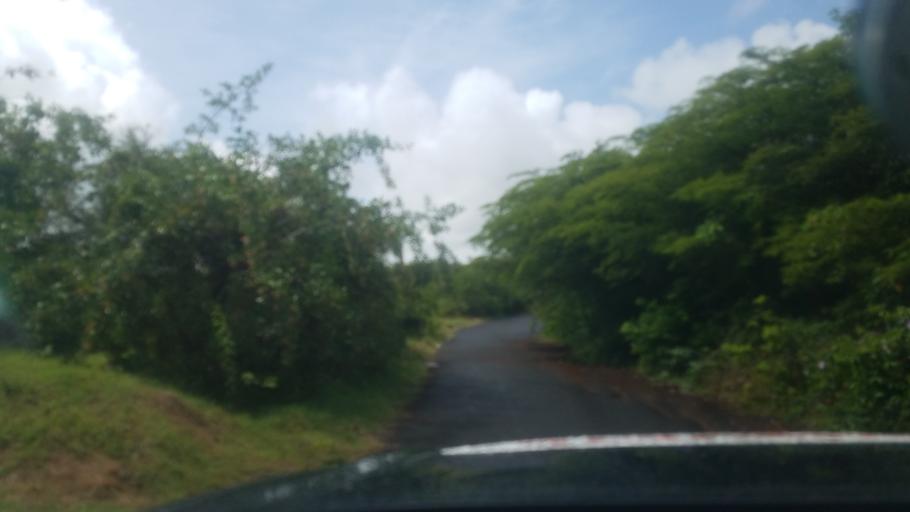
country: LC
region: Laborie Quarter
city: Laborie
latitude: 13.7345
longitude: -60.9748
